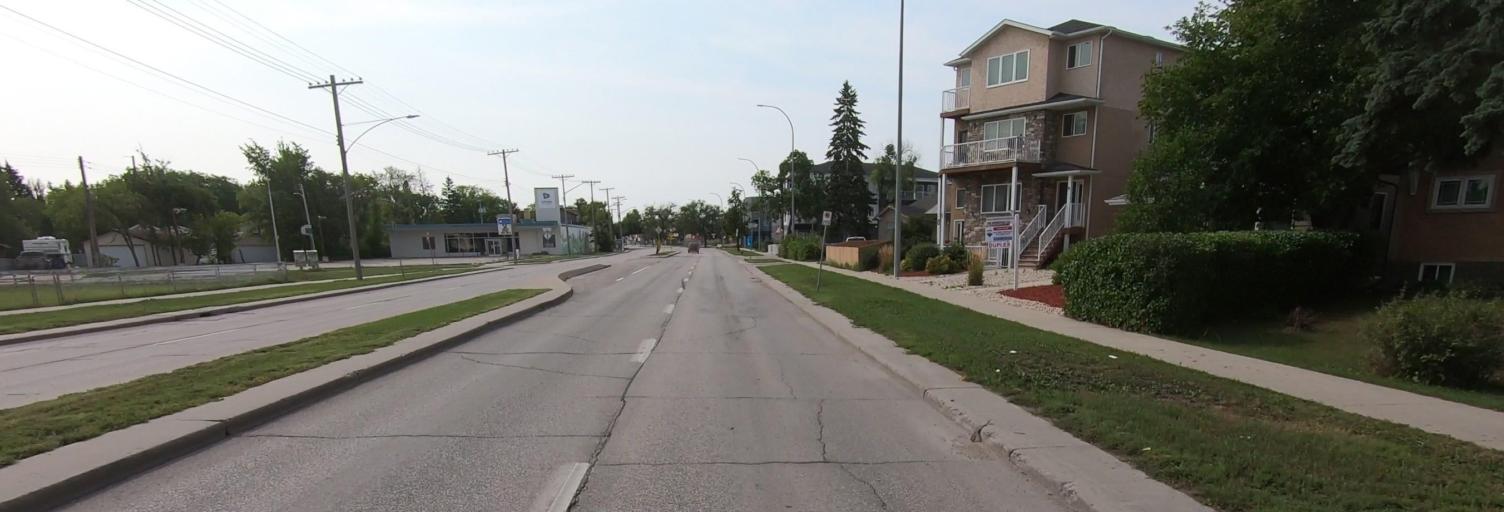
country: CA
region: Manitoba
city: Winnipeg
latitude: 49.8476
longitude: -97.1127
